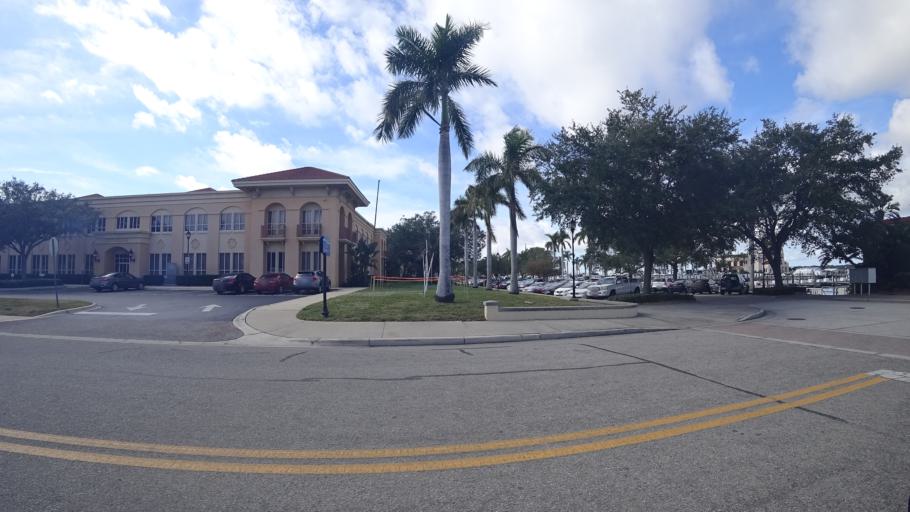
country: US
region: Florida
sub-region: Manatee County
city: Bradenton
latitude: 27.4989
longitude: -82.5719
